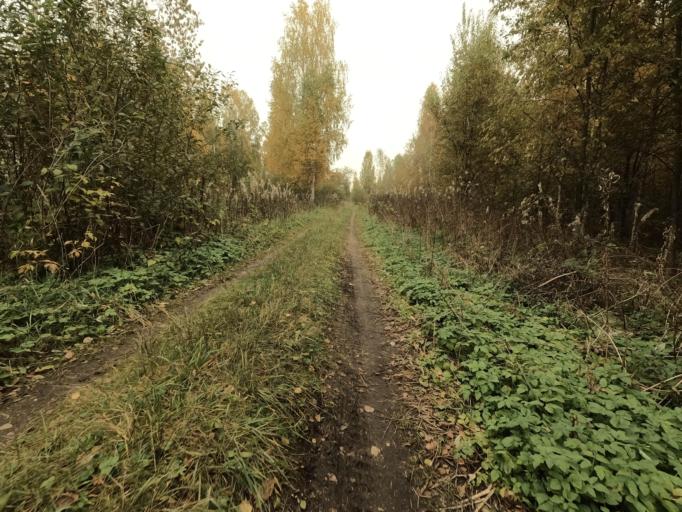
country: RU
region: Novgorod
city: Pankovka
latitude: 58.8744
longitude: 30.9391
